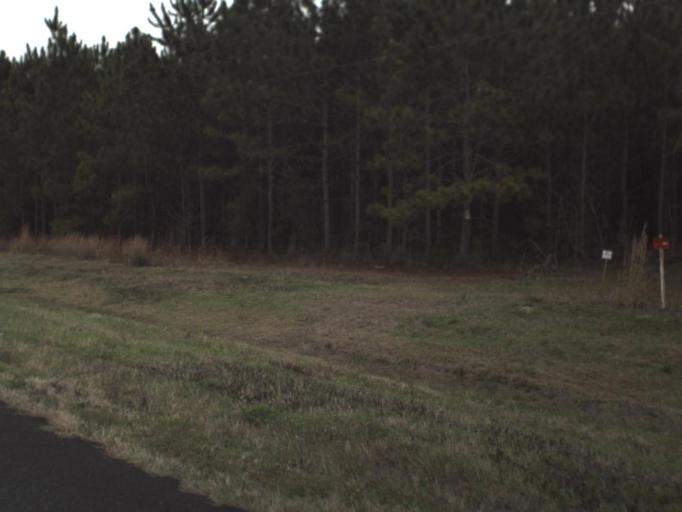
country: US
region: Florida
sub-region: Jefferson County
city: Monticello
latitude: 30.3882
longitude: -83.8491
